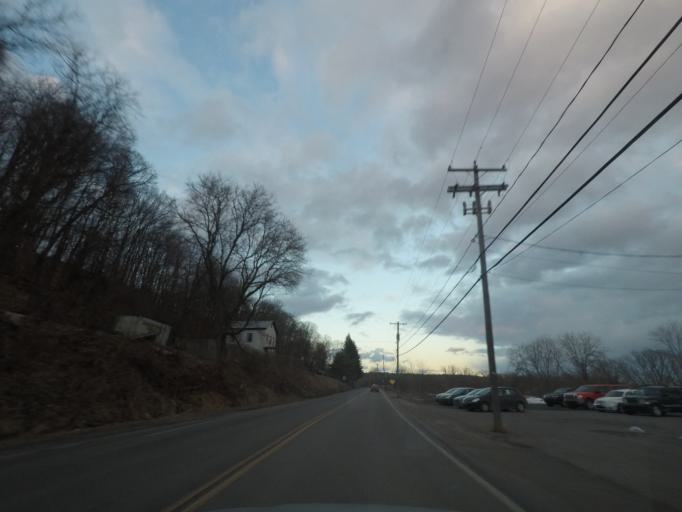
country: US
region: New York
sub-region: Montgomery County
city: Fonda
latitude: 42.9520
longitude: -74.3858
